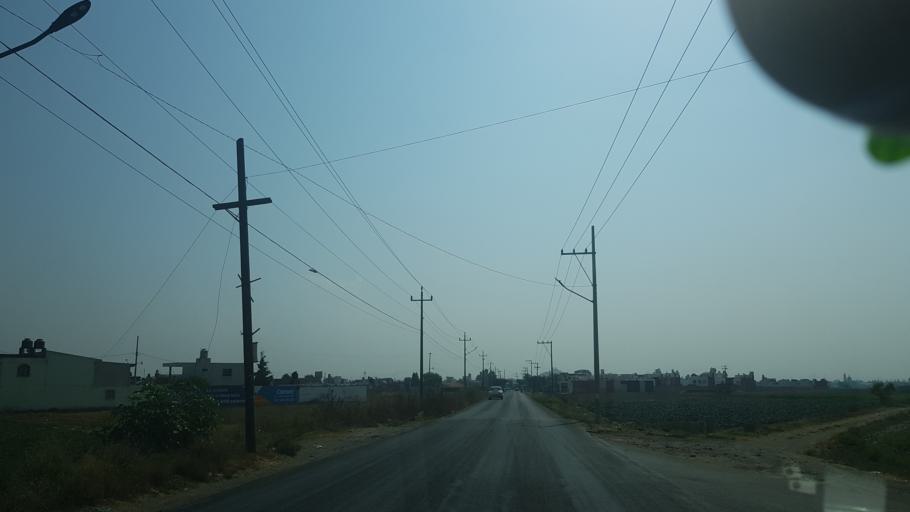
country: MX
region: Puebla
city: Cholula
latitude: 19.0550
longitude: -98.3318
